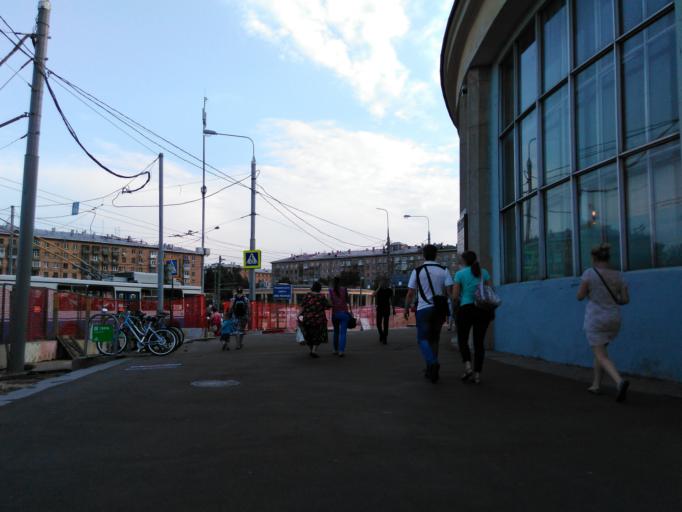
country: RU
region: Moskovskaya
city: Semenovskoye
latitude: 55.6934
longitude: 37.5349
